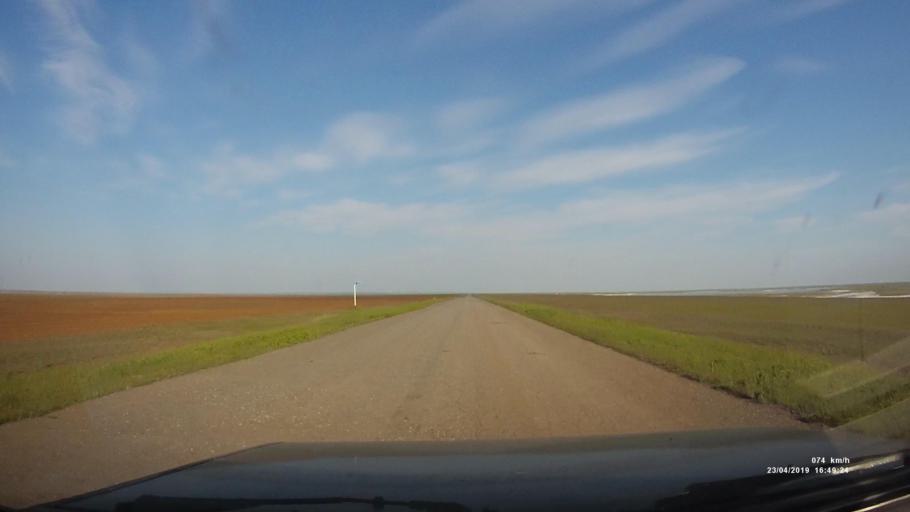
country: RU
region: Kalmykiya
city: Priyutnoye
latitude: 46.3312
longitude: 43.2760
